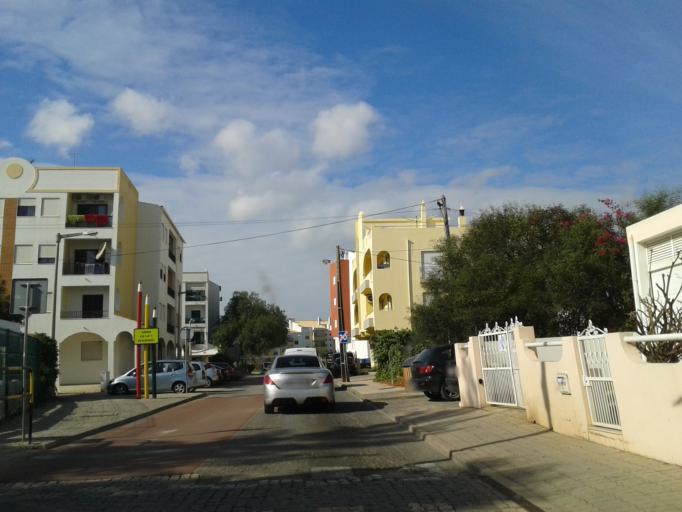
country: PT
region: Faro
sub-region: Loule
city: Almancil
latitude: 37.0890
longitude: -8.0305
